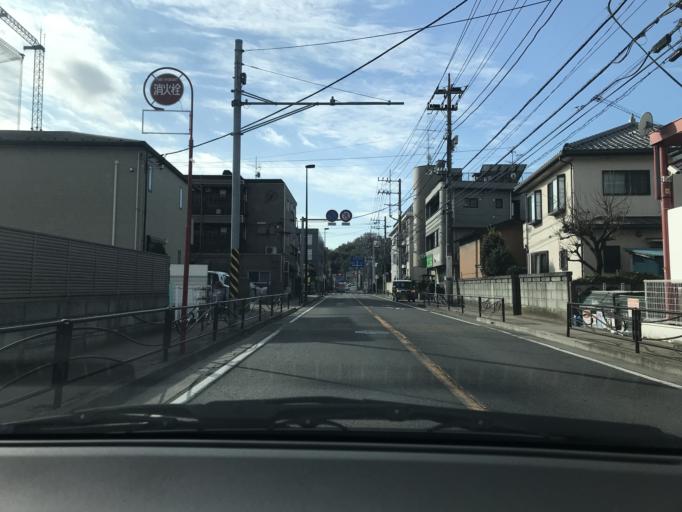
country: JP
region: Tokyo
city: Chofugaoka
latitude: 35.6137
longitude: 139.5766
